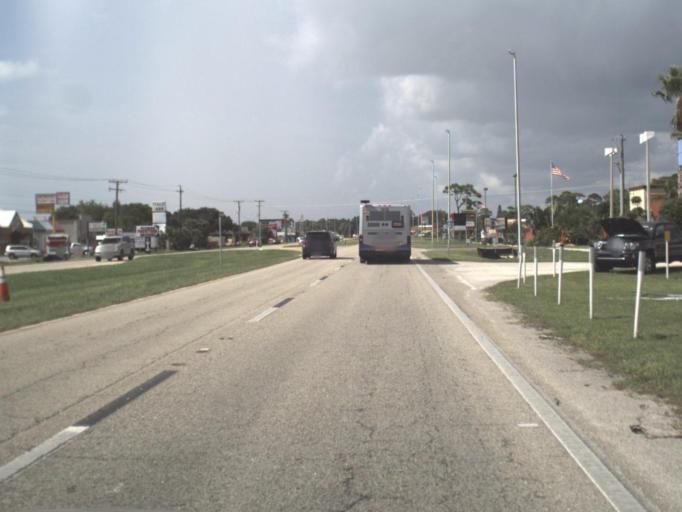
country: US
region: Florida
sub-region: Sarasota County
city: Gulf Gate Estates
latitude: 27.2483
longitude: -82.5125
